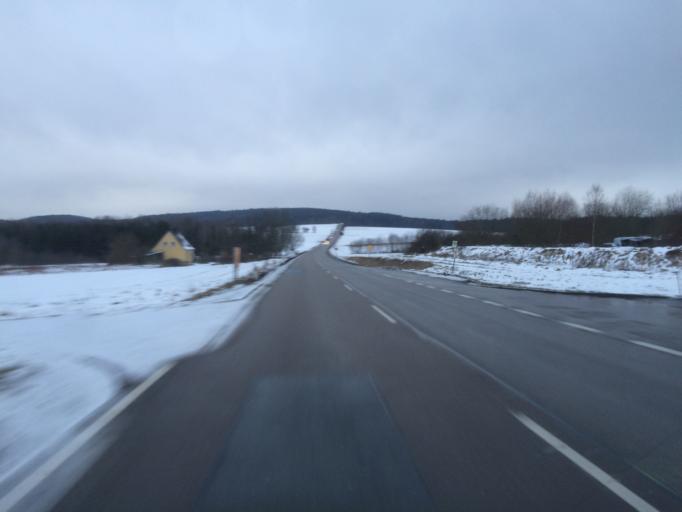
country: DE
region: Bavaria
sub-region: Upper Palatinate
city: Breitenbrunn
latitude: 49.3521
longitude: 12.0656
